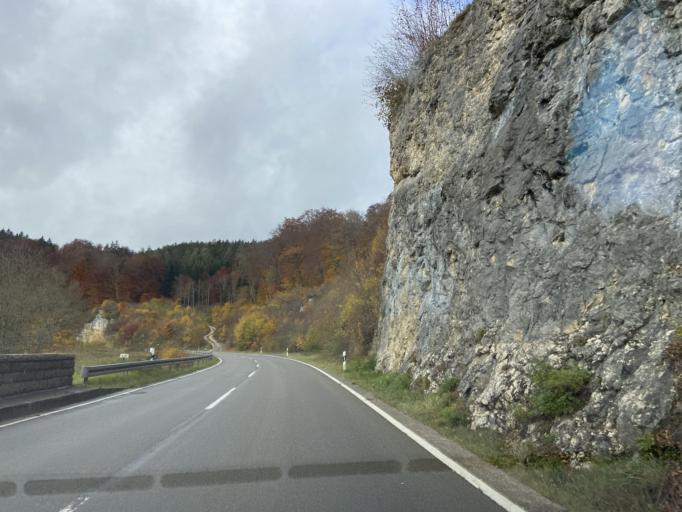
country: DE
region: Baden-Wuerttemberg
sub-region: Tuebingen Region
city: Inzigkofen
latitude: 48.0809
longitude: 9.1730
